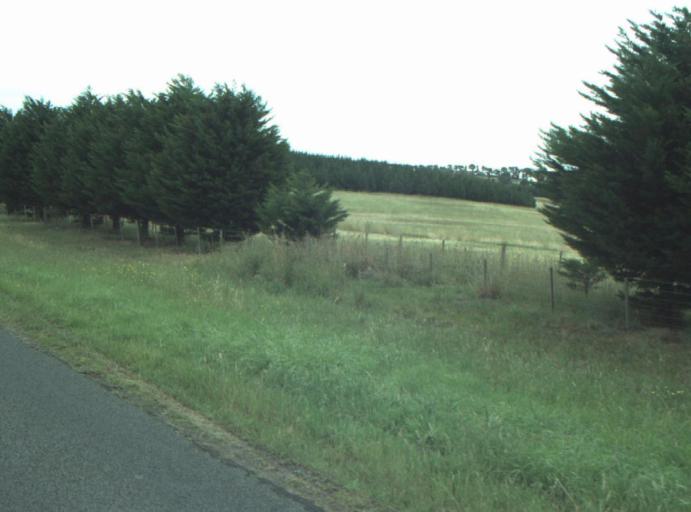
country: AU
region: Victoria
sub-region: Greater Geelong
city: Leopold
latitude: -38.2011
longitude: 144.5092
